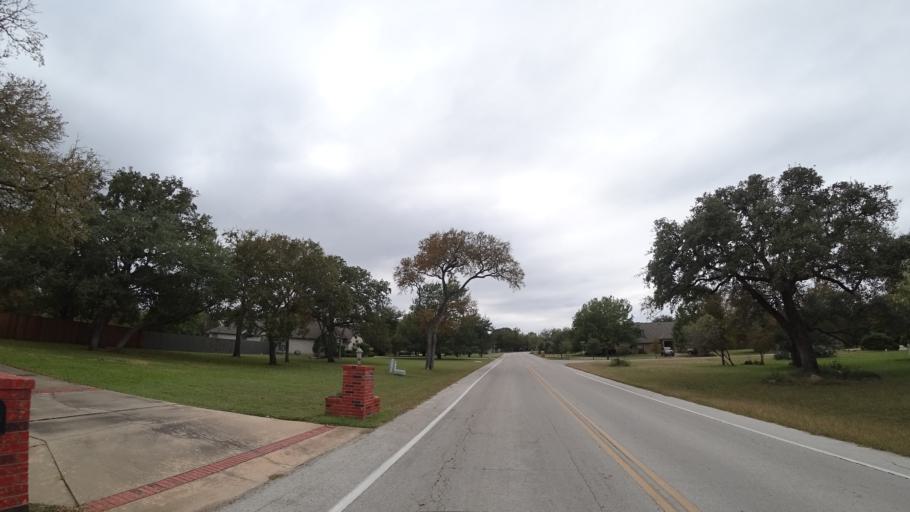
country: US
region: Texas
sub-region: Travis County
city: Shady Hollow
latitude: 30.1552
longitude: -97.8686
